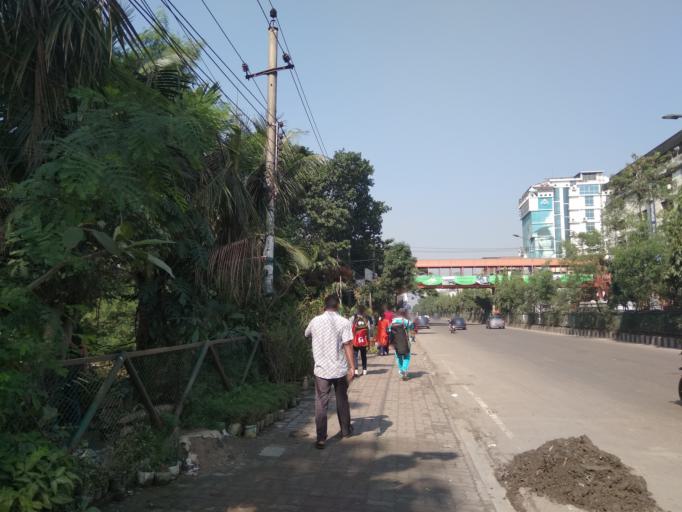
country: BD
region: Dhaka
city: Azimpur
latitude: 23.7478
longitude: 90.3801
